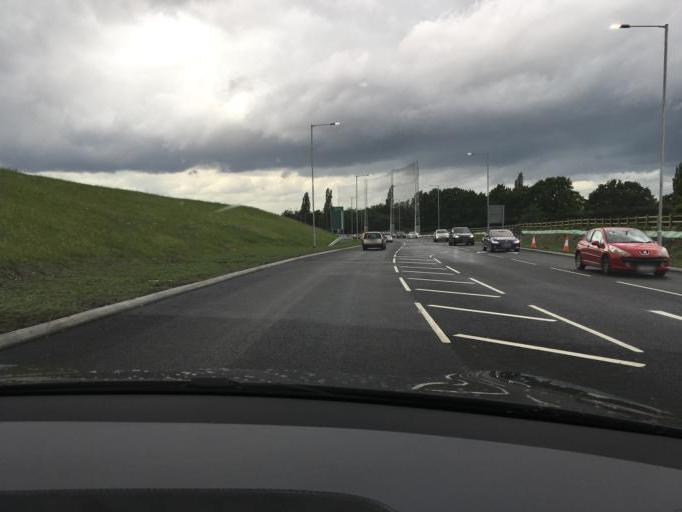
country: GB
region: England
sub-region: Borough of Stockport
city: Hazel Grove
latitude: 53.3679
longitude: -2.0941
